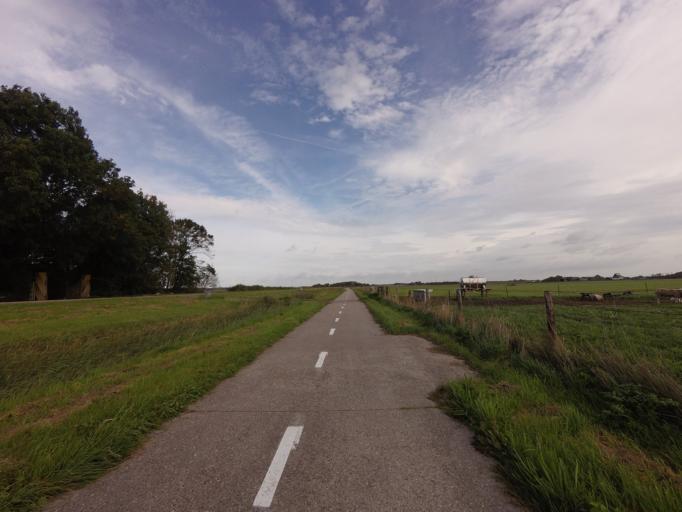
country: NL
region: North Holland
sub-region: Gemeente Texel
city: Den Burg
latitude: 53.0297
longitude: 4.7828
